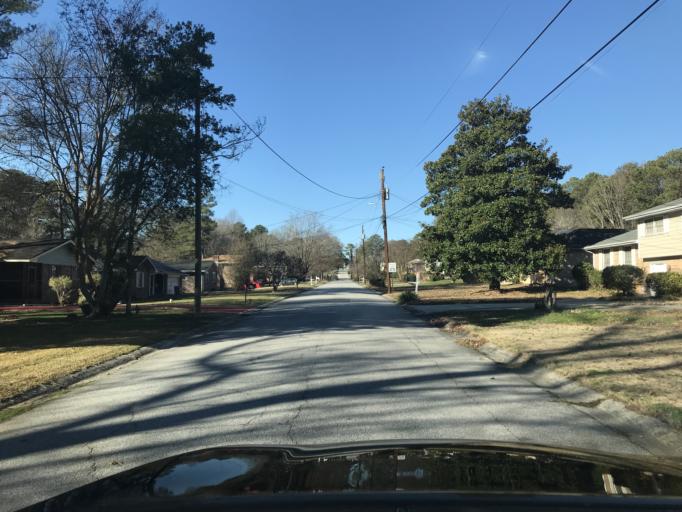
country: US
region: Georgia
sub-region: Clayton County
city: Morrow
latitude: 33.5665
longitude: -84.3636
